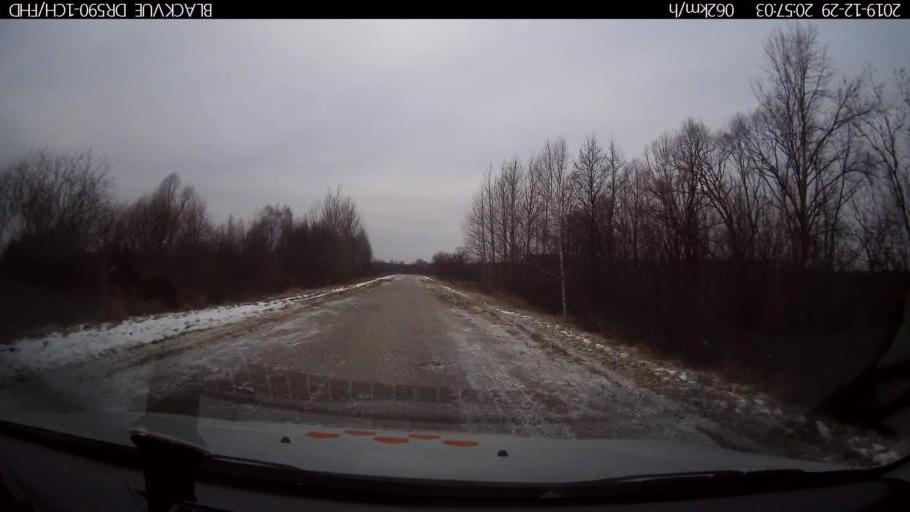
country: RU
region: Nizjnij Novgorod
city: Afonino
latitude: 56.1576
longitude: 43.9947
